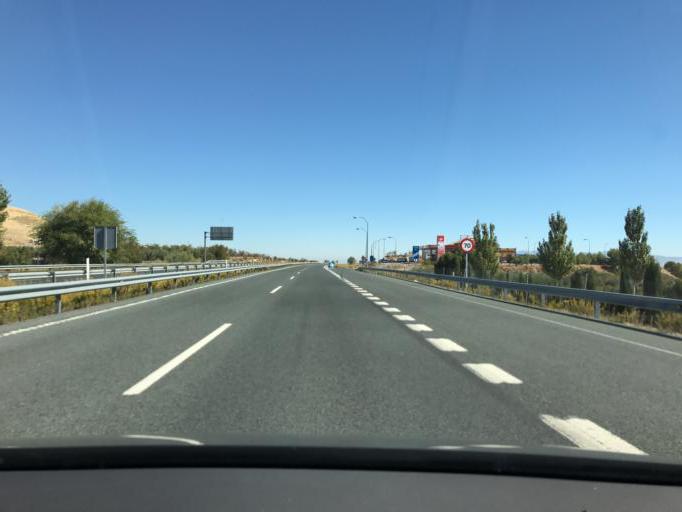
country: ES
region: Andalusia
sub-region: Provincia de Granada
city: Diezma
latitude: 37.3176
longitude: -3.3271
